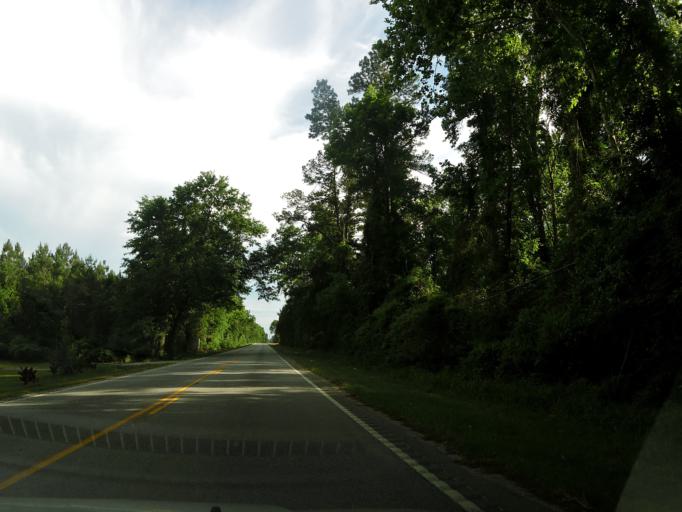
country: US
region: South Carolina
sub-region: Allendale County
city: Fairfax
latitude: 32.8577
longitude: -81.2381
